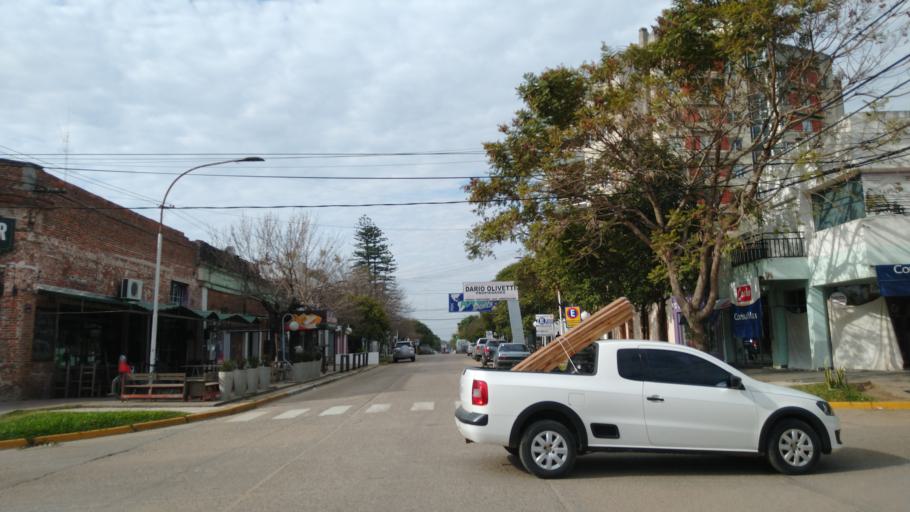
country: AR
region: Entre Rios
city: Chajari
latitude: -30.7578
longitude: -57.9861
